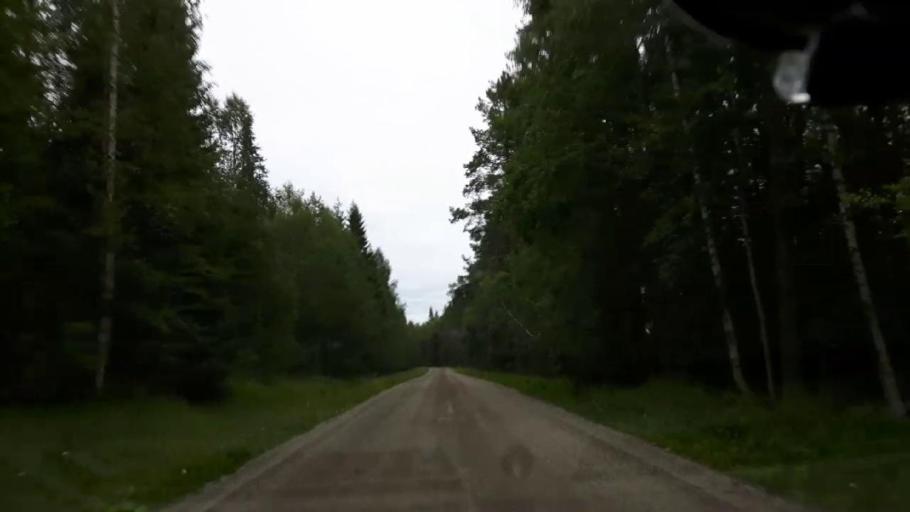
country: SE
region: Jaemtland
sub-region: Braecke Kommun
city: Braecke
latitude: 62.9839
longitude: 15.3920
